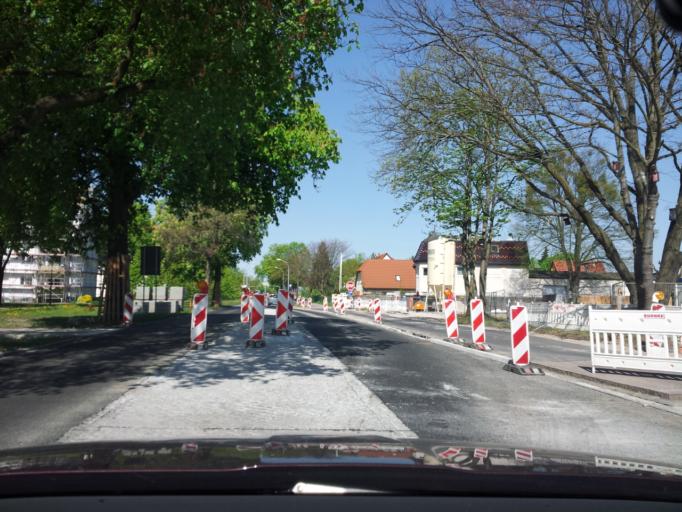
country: DE
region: Brandenburg
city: Teltow
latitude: 52.3958
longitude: 13.2805
